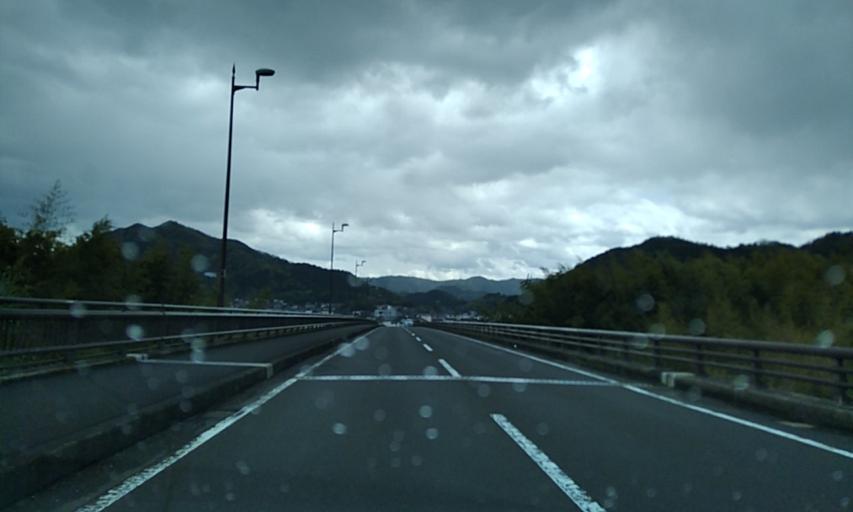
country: JP
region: Kyoto
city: Ayabe
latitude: 35.3079
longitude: 135.2304
